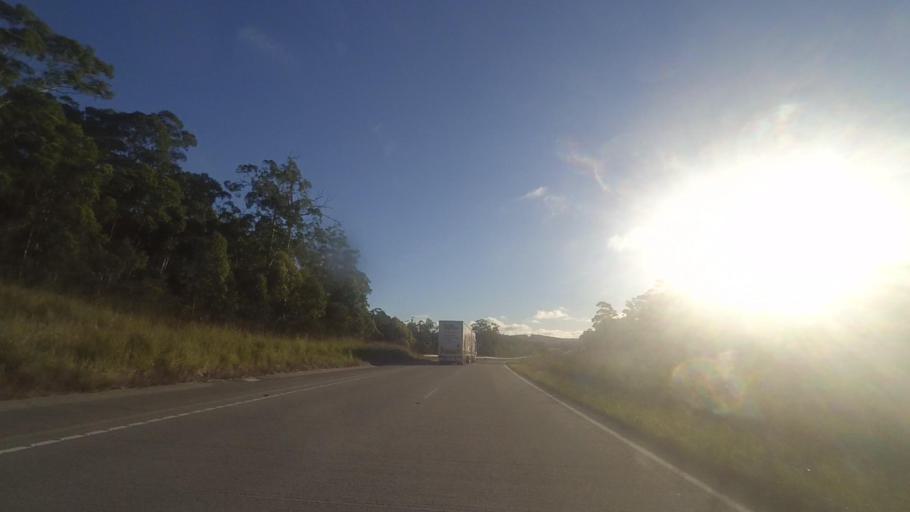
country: AU
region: New South Wales
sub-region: Great Lakes
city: Bulahdelah
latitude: -32.5167
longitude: 152.2086
